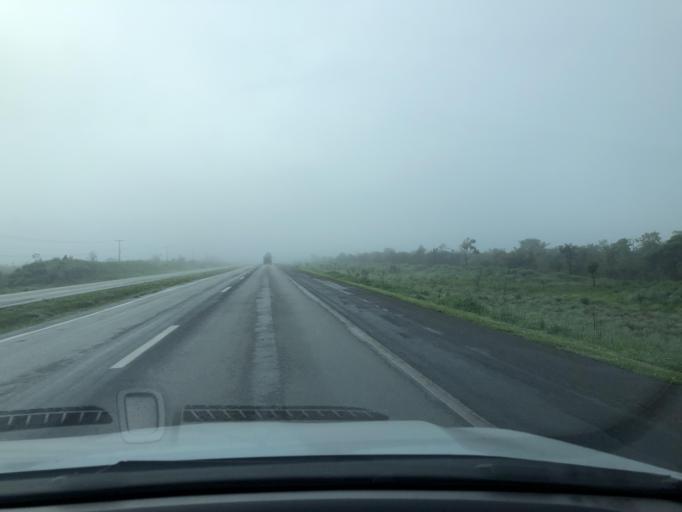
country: BR
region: Goias
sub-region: Luziania
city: Luziania
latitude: -16.2883
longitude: -47.8546
